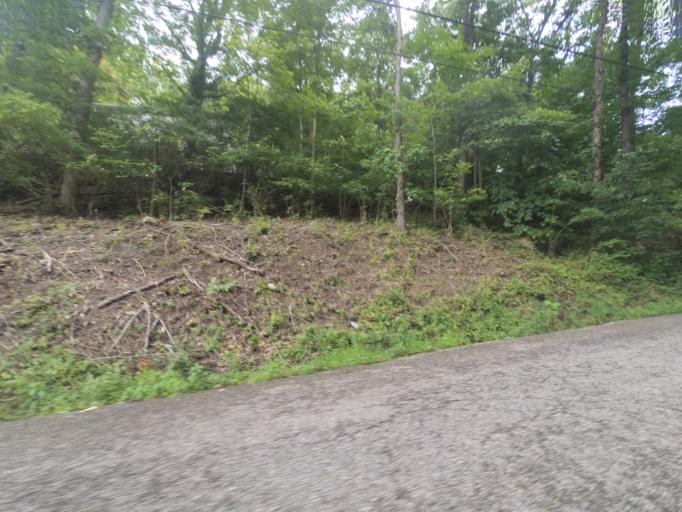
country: US
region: West Virginia
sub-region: Cabell County
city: Huntington
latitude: 38.4018
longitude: -82.4611
